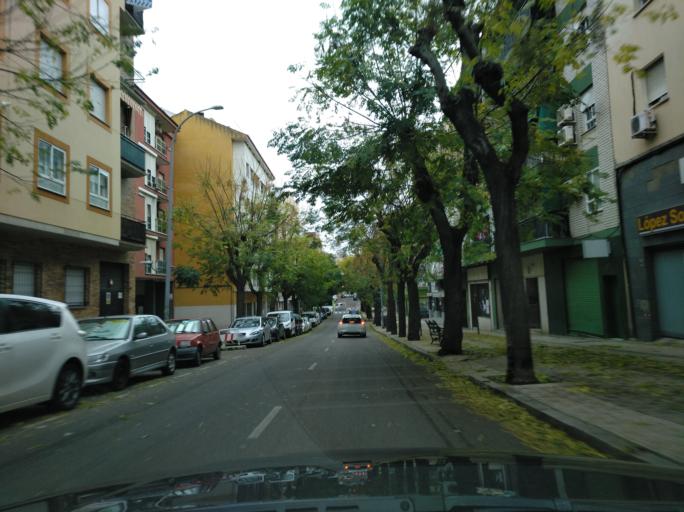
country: ES
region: Extremadura
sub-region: Provincia de Badajoz
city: Badajoz
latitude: 38.8870
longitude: -6.9793
